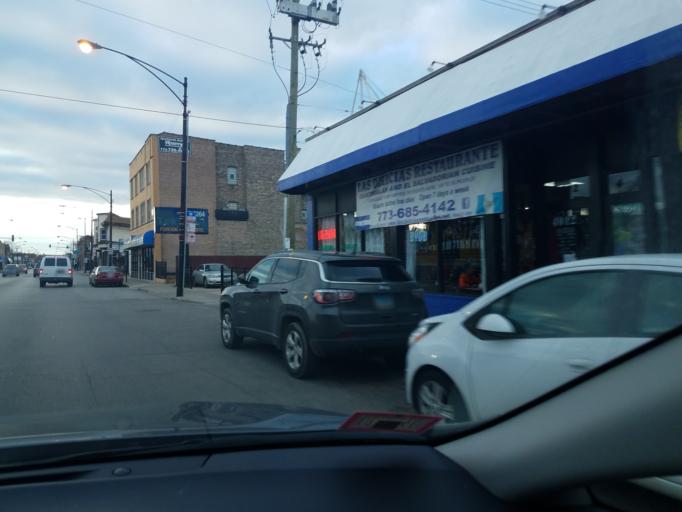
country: US
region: Illinois
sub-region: Cook County
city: Lincolnwood
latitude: 41.9610
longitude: -87.7282
